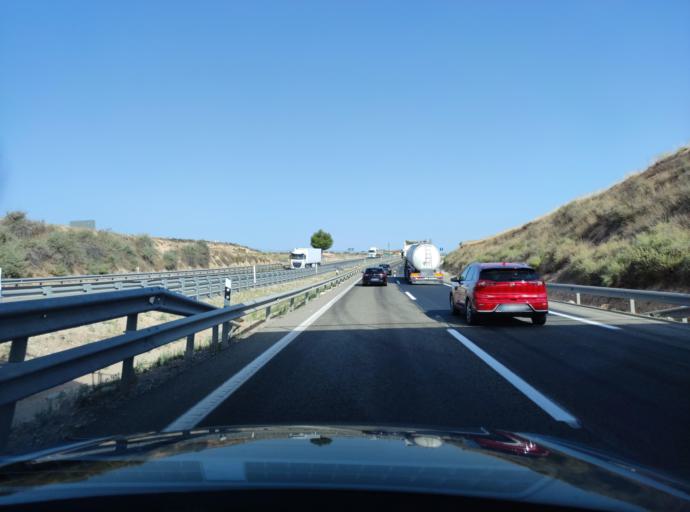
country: ES
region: Valencia
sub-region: Provincia de Alicante
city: Sax
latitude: 38.5482
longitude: -0.8159
